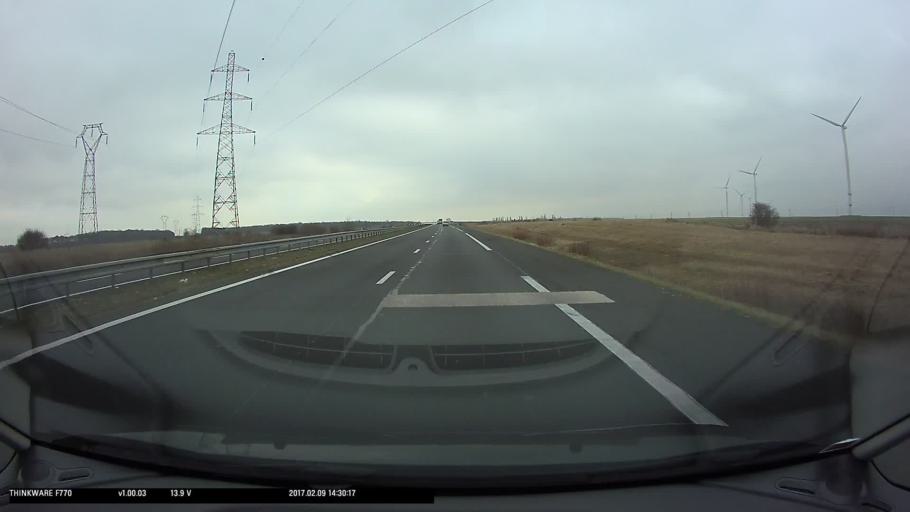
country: FR
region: Centre
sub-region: Departement du Cher
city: Mehun-sur-Yevre
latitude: 47.1031
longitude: 2.2183
